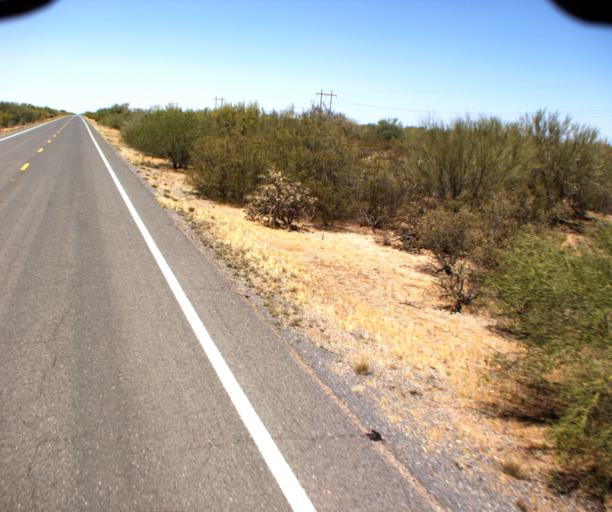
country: US
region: Arizona
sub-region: Pinal County
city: Florence
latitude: 32.8076
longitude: -111.1897
